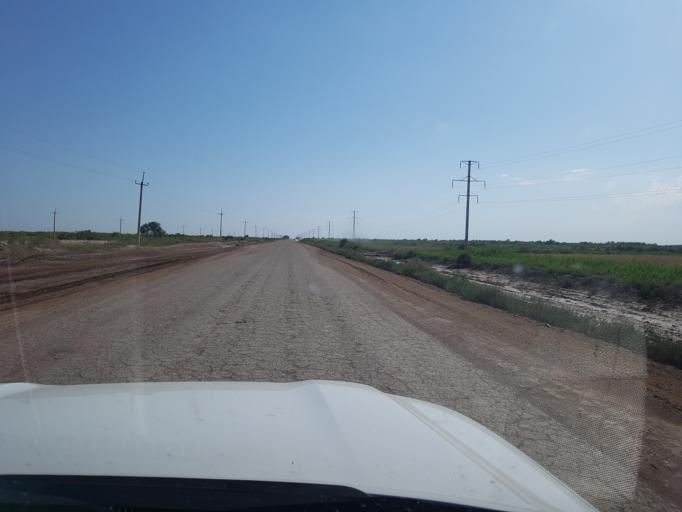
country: TM
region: Dasoguz
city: Koeneuergench
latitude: 42.1186
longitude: 58.9288
